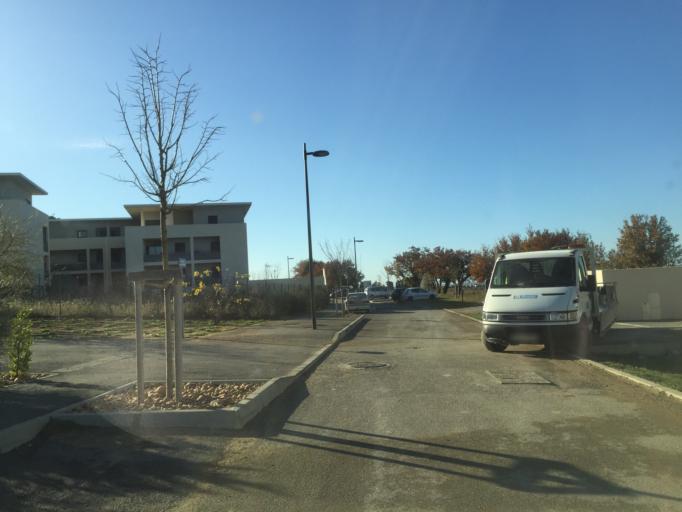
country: FR
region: Provence-Alpes-Cote d'Azur
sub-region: Departement du Vaucluse
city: Bedarrides
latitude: 44.0337
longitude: 4.8957
